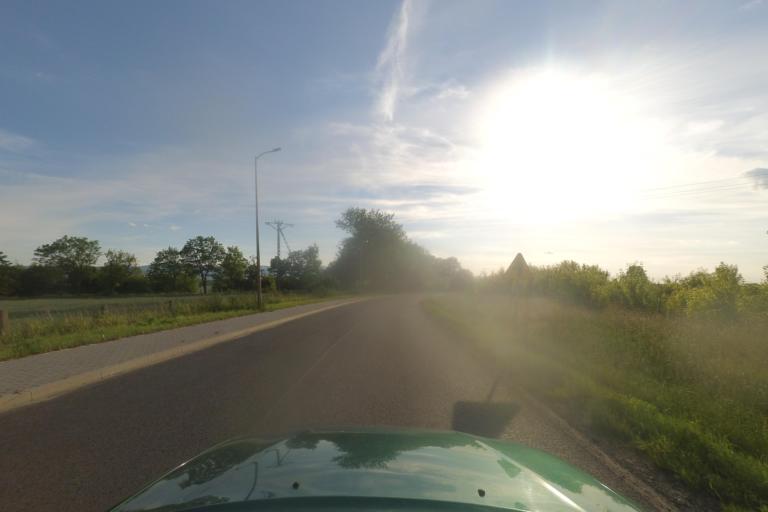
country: PL
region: Lower Silesian Voivodeship
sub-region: Powiat dzierzoniowski
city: Uciechow
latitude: 50.7317
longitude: 16.6929
